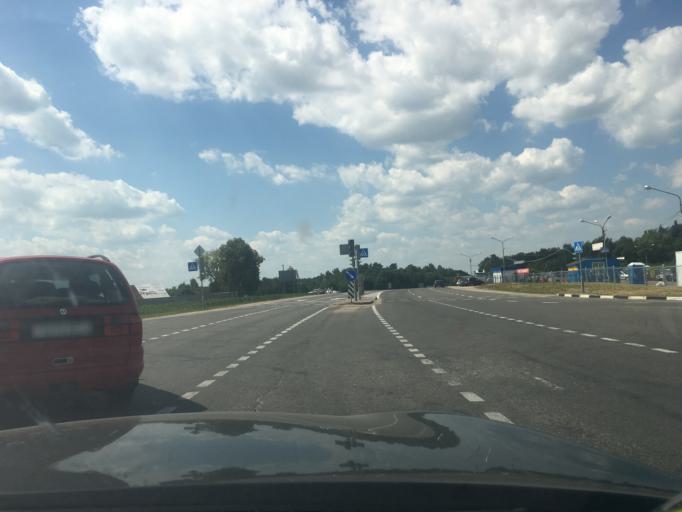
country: BY
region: Grodnenskaya
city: Hrodna
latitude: 53.6186
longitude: 23.8718
